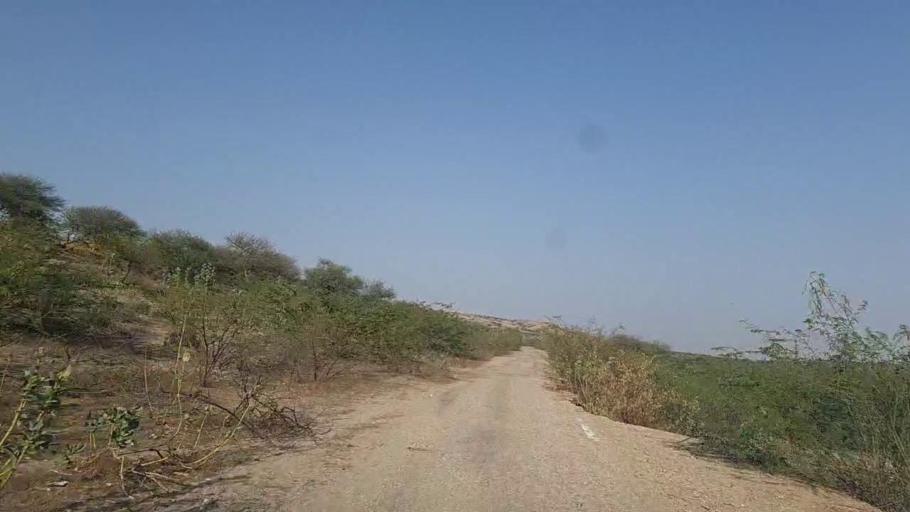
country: PK
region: Sindh
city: Naukot
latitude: 24.6130
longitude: 69.3436
